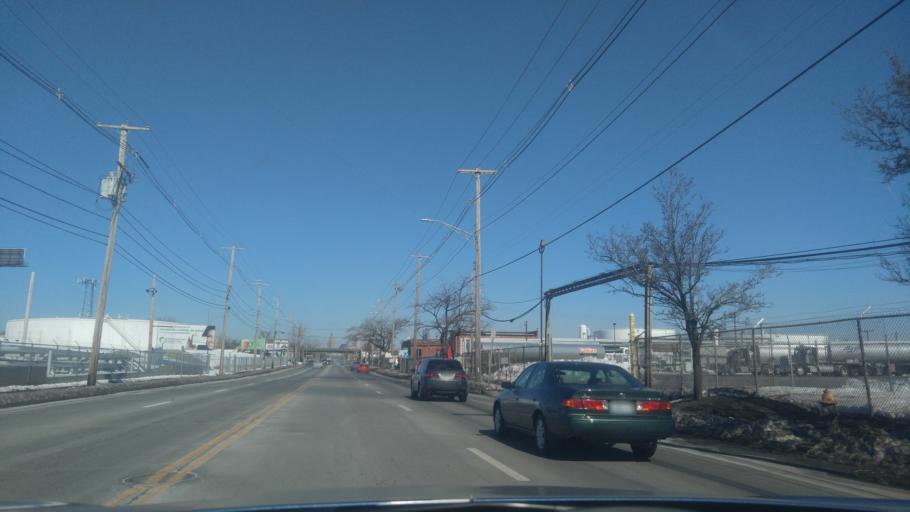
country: US
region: Rhode Island
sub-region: Providence County
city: Providence
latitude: 41.7983
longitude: -71.3993
